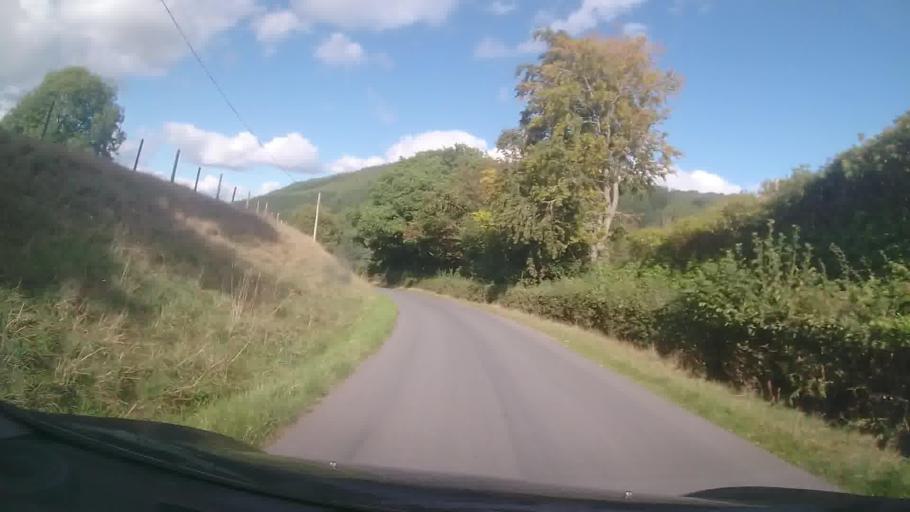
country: GB
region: Wales
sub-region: Sir Powys
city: Brecon
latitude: 51.8770
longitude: -3.3027
